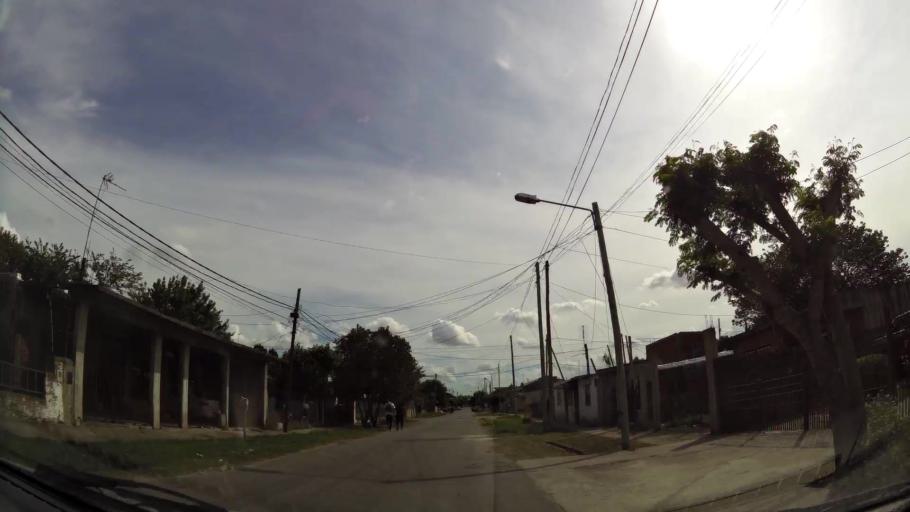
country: AR
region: Buenos Aires
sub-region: Partido de Quilmes
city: Quilmes
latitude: -34.7655
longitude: -58.2428
